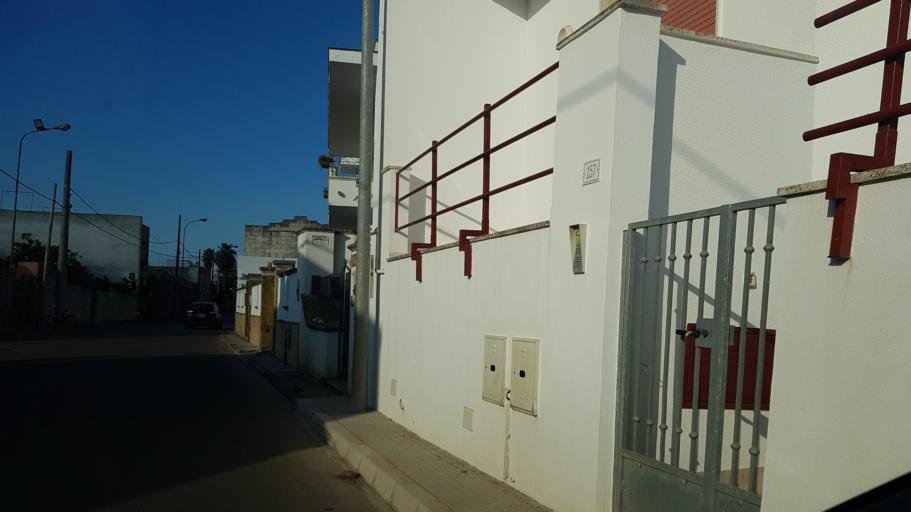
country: IT
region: Apulia
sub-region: Provincia di Lecce
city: Castiglione
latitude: 39.9802
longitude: 18.3438
